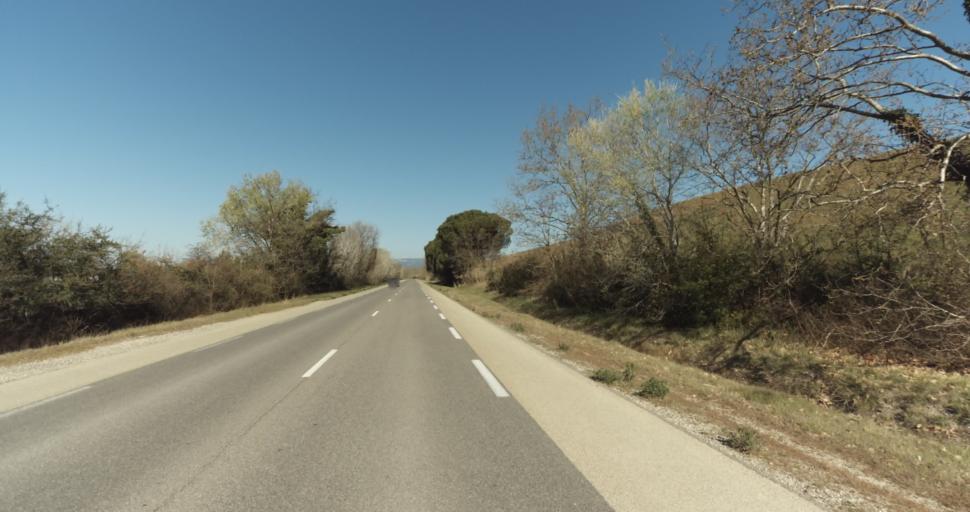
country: FR
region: Provence-Alpes-Cote d'Azur
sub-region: Departement du Vaucluse
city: Lauris
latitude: 43.7211
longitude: 5.3304
